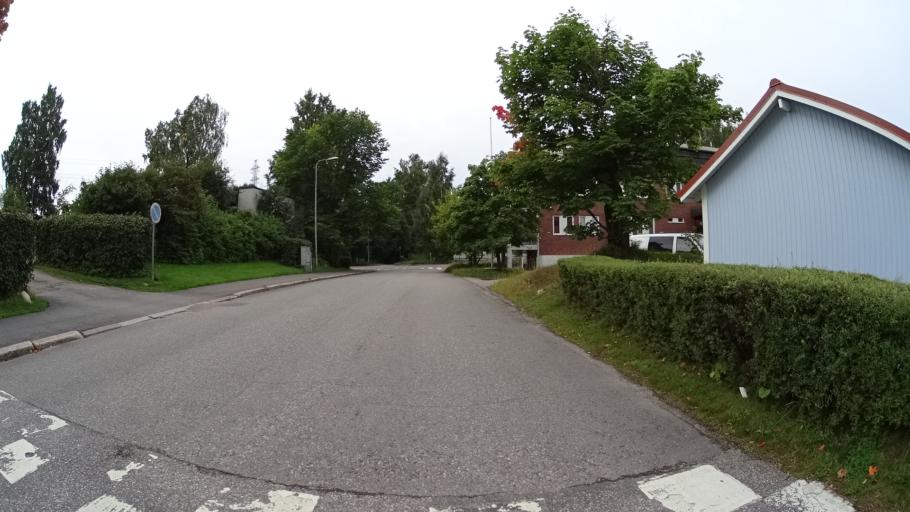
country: FI
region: Uusimaa
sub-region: Helsinki
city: Helsinki
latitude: 60.2219
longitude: 24.9355
